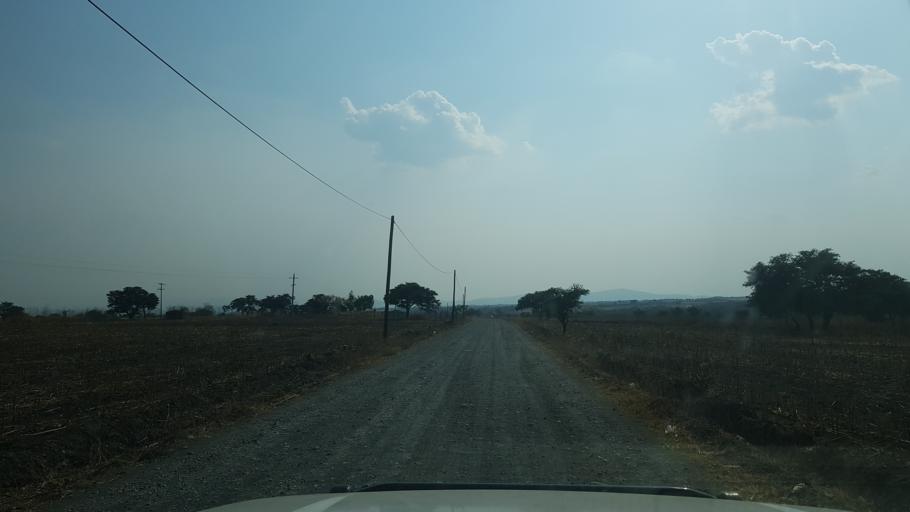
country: MX
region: Morelos
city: Tlacotepec
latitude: 18.7769
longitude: -98.7303
